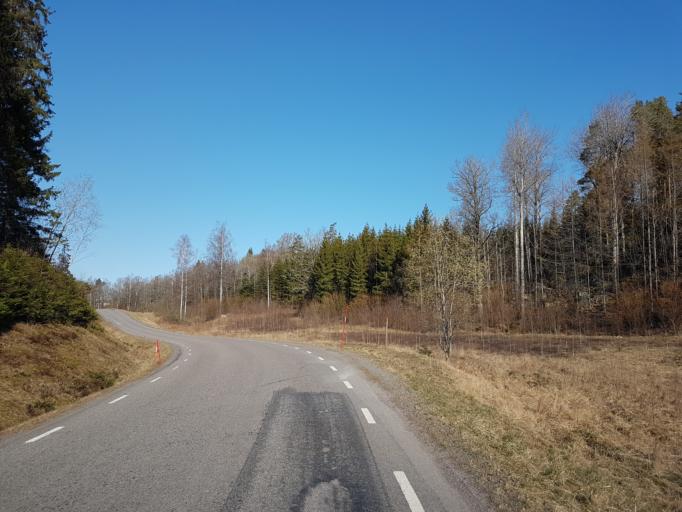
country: SE
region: OEstergoetland
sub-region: Valdemarsviks Kommun
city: Gusum
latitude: 58.1894
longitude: 16.2993
